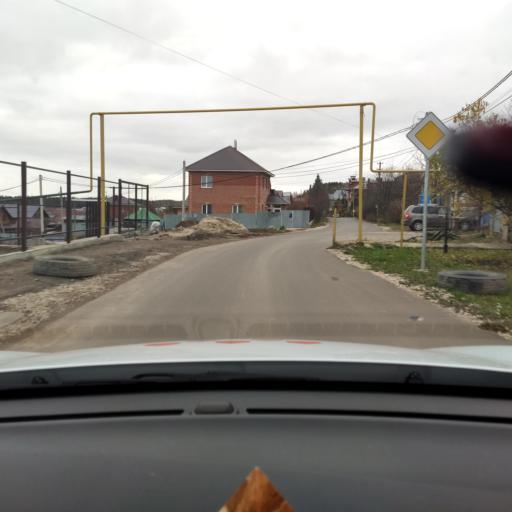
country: RU
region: Tatarstan
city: Vysokaya Gora
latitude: 55.8725
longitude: 49.2545
